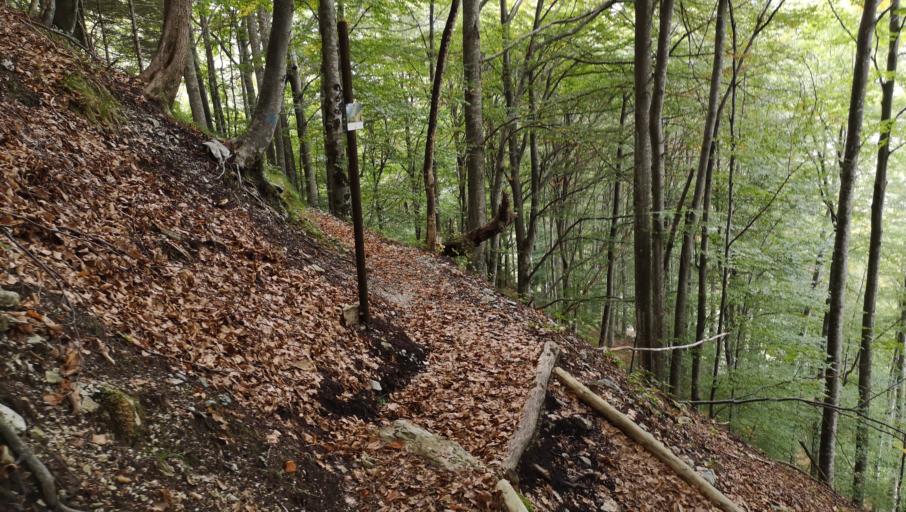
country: IT
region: Friuli Venezia Giulia
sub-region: Provincia di Udine
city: Pontebba
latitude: 46.5222
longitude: 13.2978
